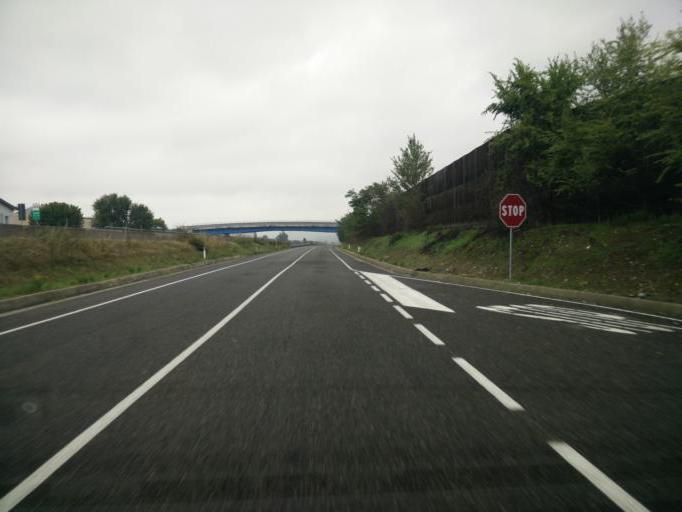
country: IT
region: Emilia-Romagna
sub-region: Provincia di Bologna
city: Borgonuovo
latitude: 44.4198
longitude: 11.2706
